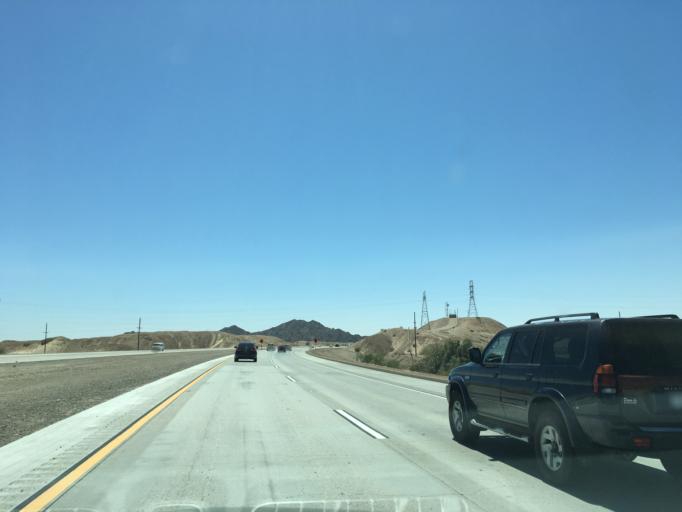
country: MX
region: Baja California
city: Los Algodones
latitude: 32.7444
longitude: -114.7085
